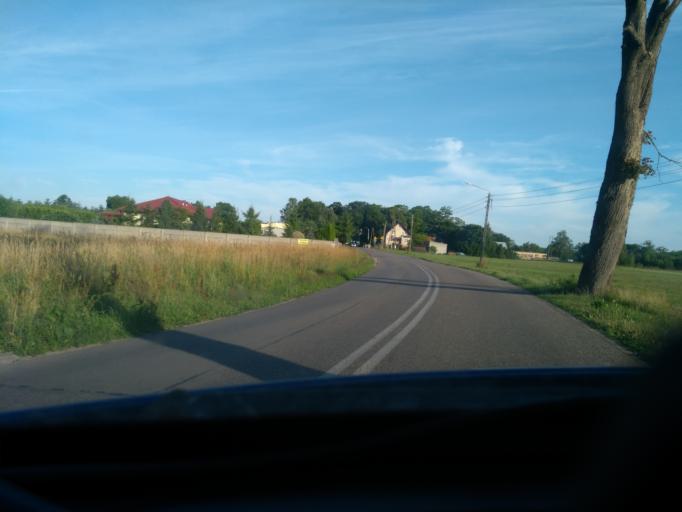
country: PL
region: Pomeranian Voivodeship
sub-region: Powiat kartuski
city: Przodkowo
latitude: 54.3985
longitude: 18.3349
